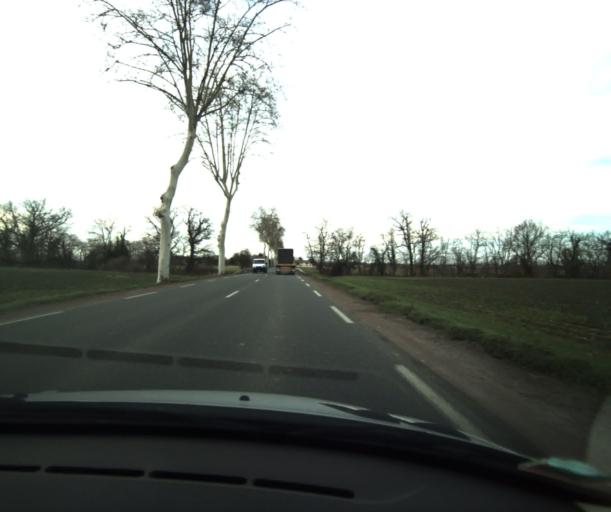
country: FR
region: Midi-Pyrenees
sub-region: Departement du Tarn-et-Garonne
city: Saint-Porquier
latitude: 44.0159
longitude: 1.1651
